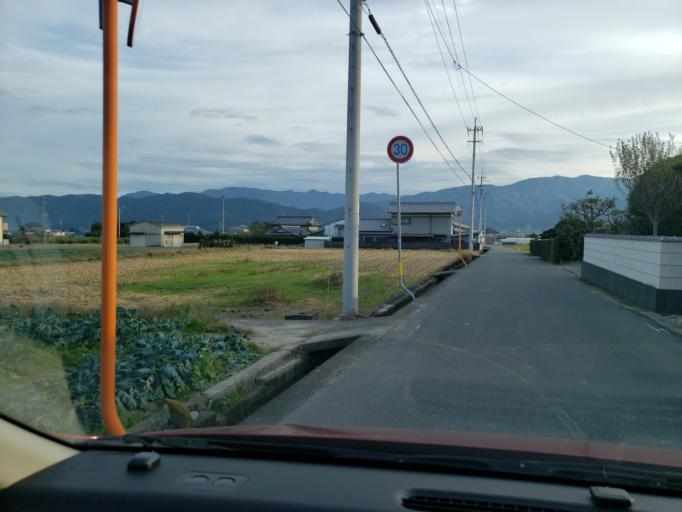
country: JP
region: Tokushima
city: Wakimachi
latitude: 34.0855
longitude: 134.2268
